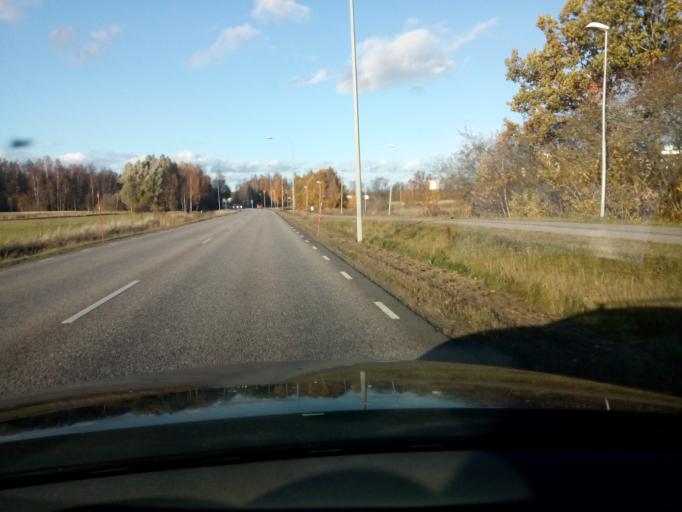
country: SE
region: Soedermanland
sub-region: Nykopings Kommun
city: Nykoping
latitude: 58.7375
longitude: 17.0056
